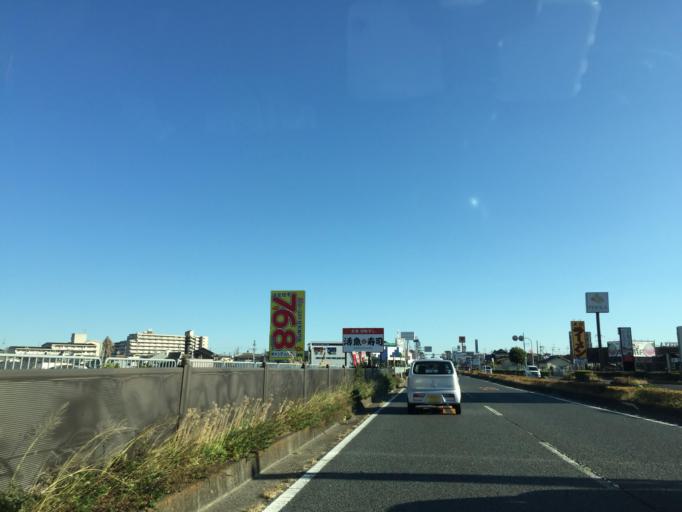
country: JP
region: Osaka
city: Kaizuka
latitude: 34.4257
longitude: 135.3430
